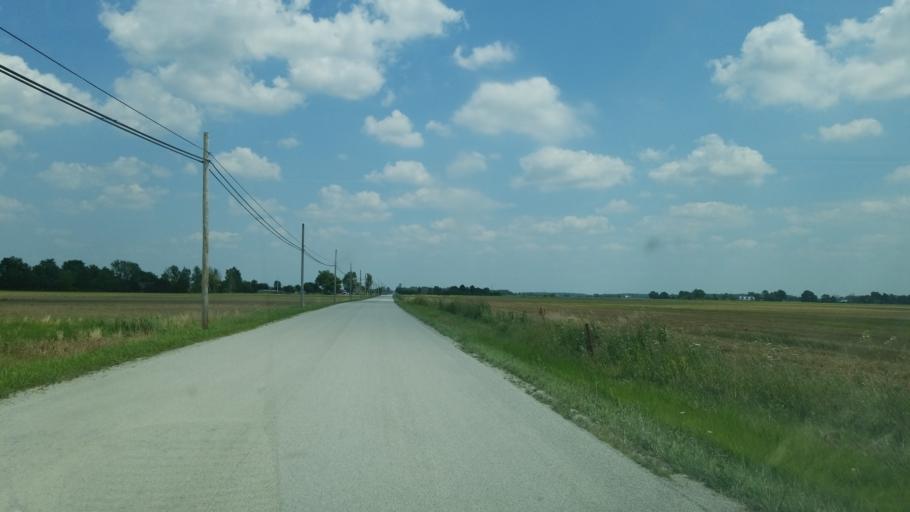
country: US
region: Ohio
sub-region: Wood County
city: North Baltimore
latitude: 41.2402
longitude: -83.6119
